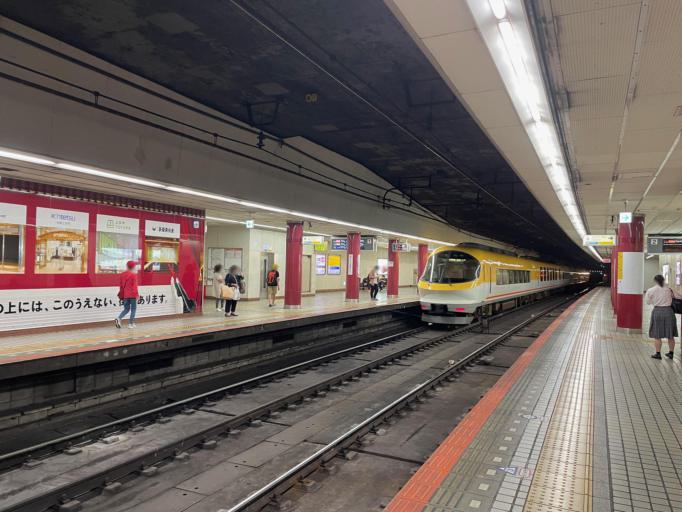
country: JP
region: Osaka
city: Osaka-shi
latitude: 34.6660
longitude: 135.5201
